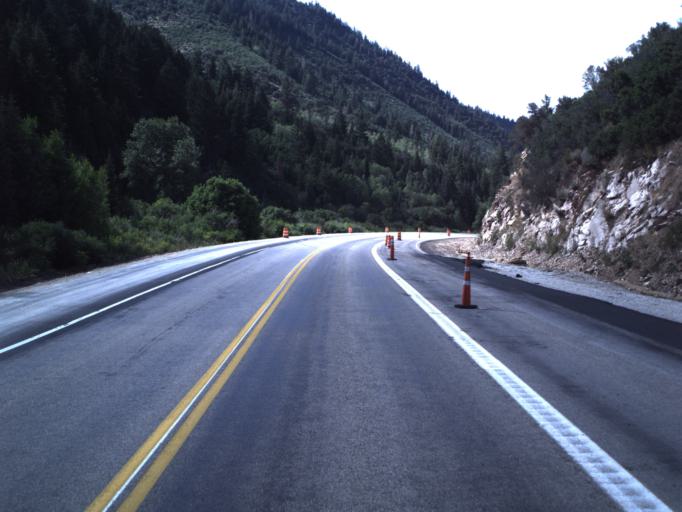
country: US
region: Utah
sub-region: Wasatch County
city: Heber
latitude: 40.3567
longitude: -111.2818
